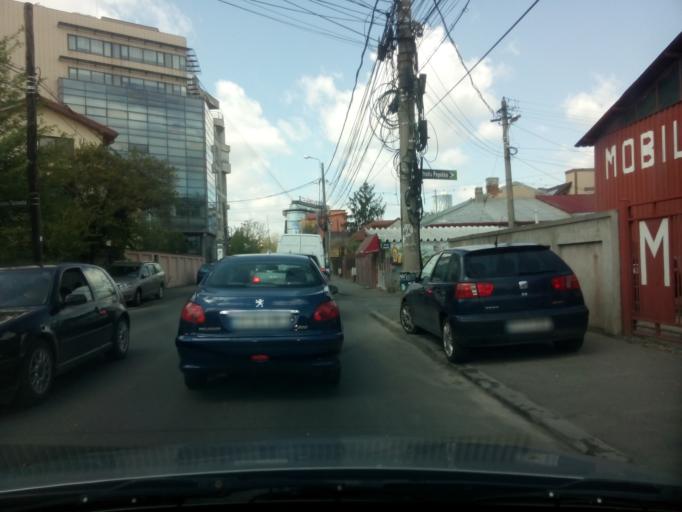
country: RO
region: Bucuresti
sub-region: Municipiul Bucuresti
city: Bucharest
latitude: 44.4692
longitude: 26.1113
